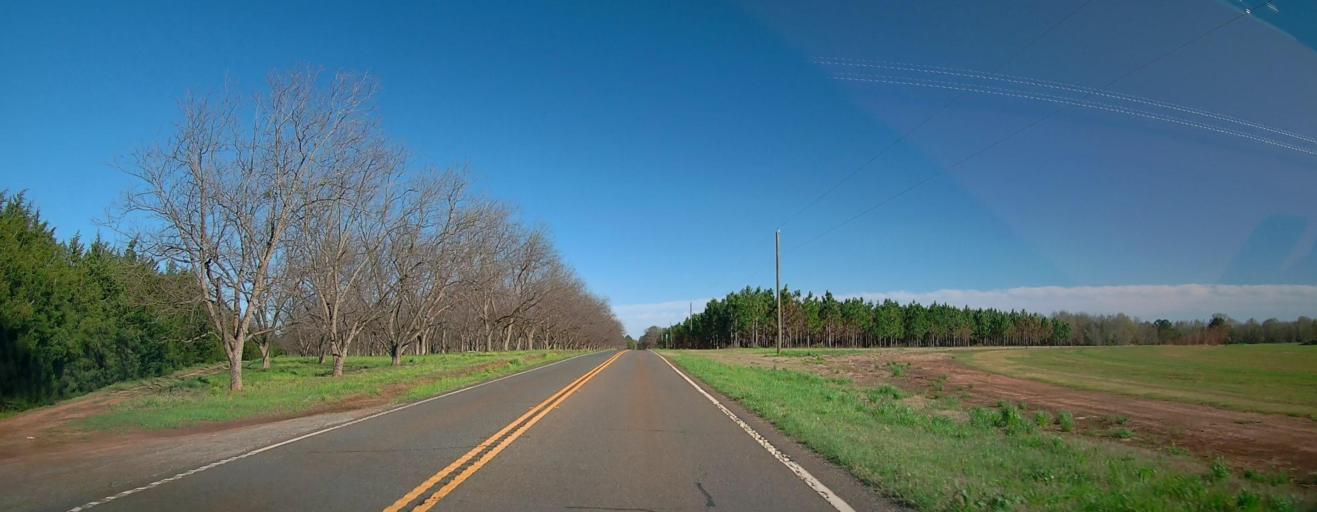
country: US
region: Georgia
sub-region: Macon County
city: Marshallville
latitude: 32.4467
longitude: -83.9030
